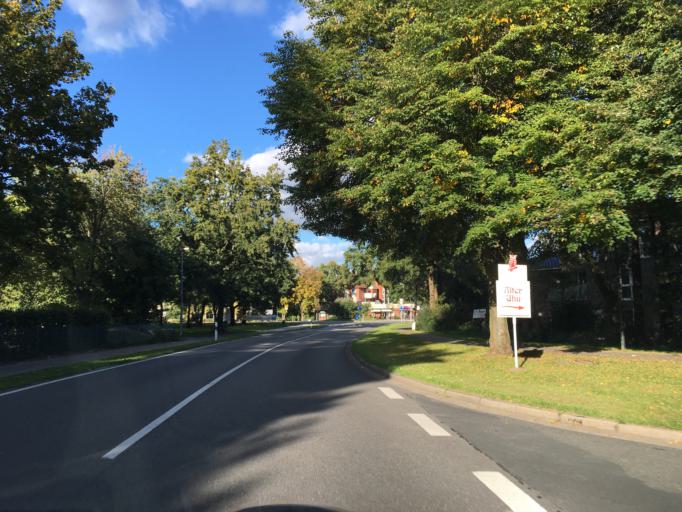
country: DE
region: Lower Saxony
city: Reppenstedt
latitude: 53.2469
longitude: 10.3525
